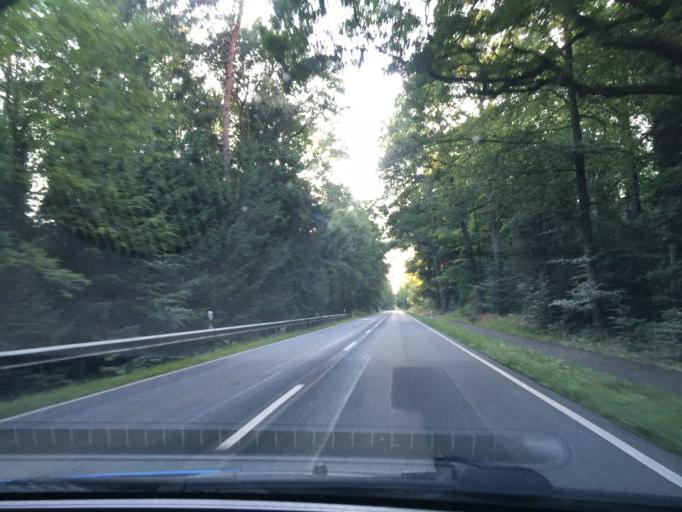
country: DE
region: Lower Saxony
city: Unterluss
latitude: 52.8168
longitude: 10.3412
